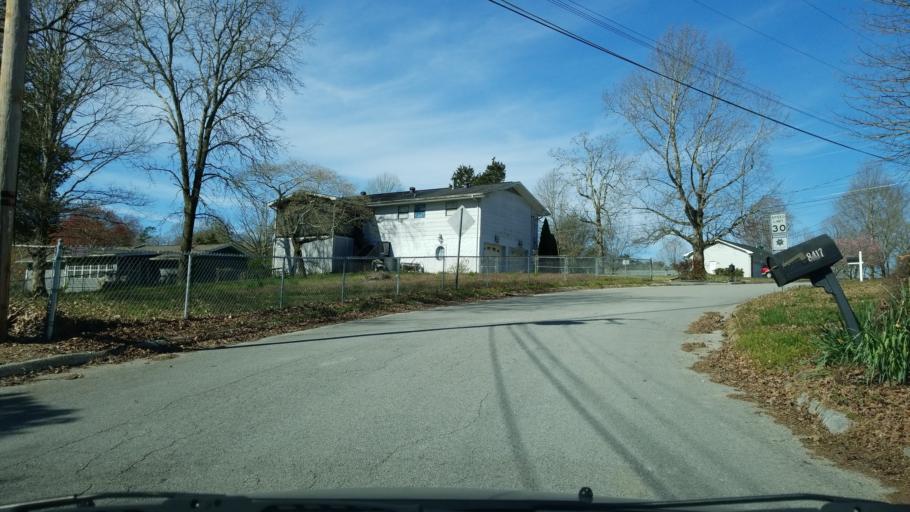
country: US
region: Tennessee
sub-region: Hamilton County
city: Collegedale
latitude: 35.0883
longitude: -85.0859
